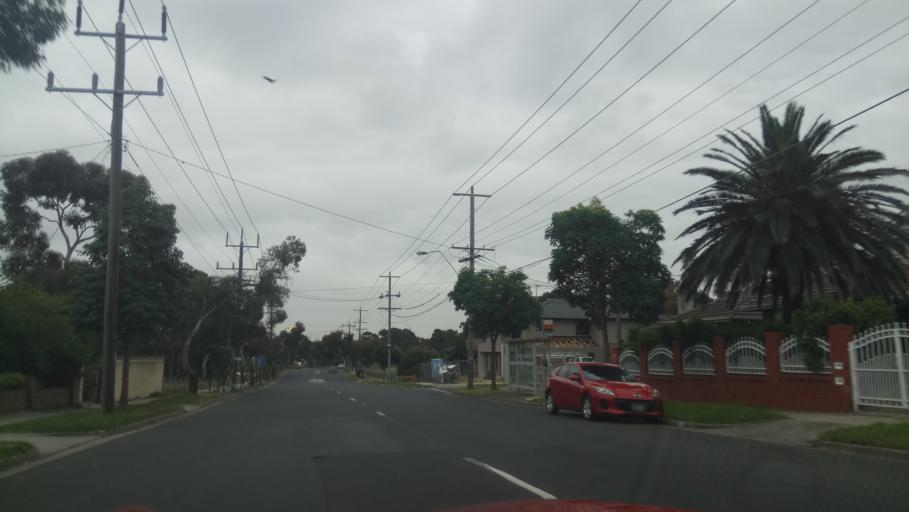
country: AU
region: Victoria
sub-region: Hobsons Bay
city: Altona North
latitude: -37.8298
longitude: 144.8354
